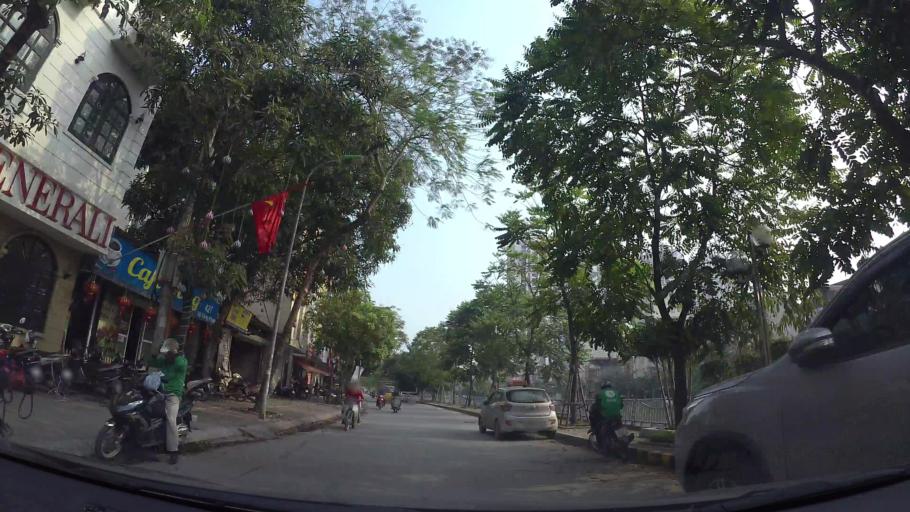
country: VN
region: Ha Noi
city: Thanh Xuan
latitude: 20.9882
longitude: 105.8135
